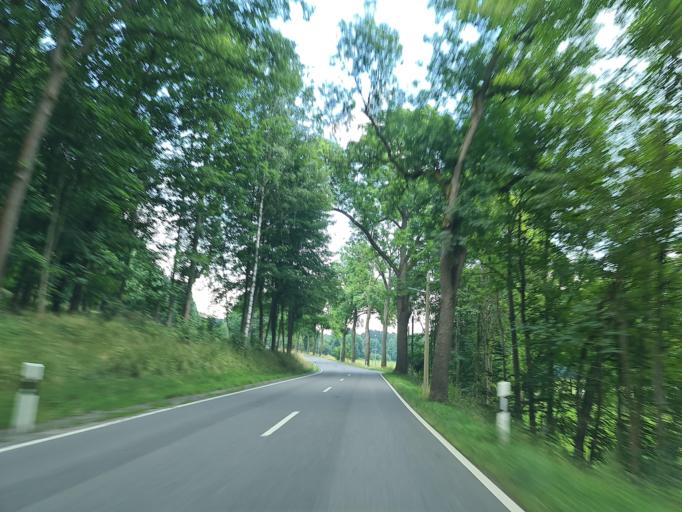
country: DE
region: Saxony
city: Bergen
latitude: 50.4663
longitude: 12.2777
